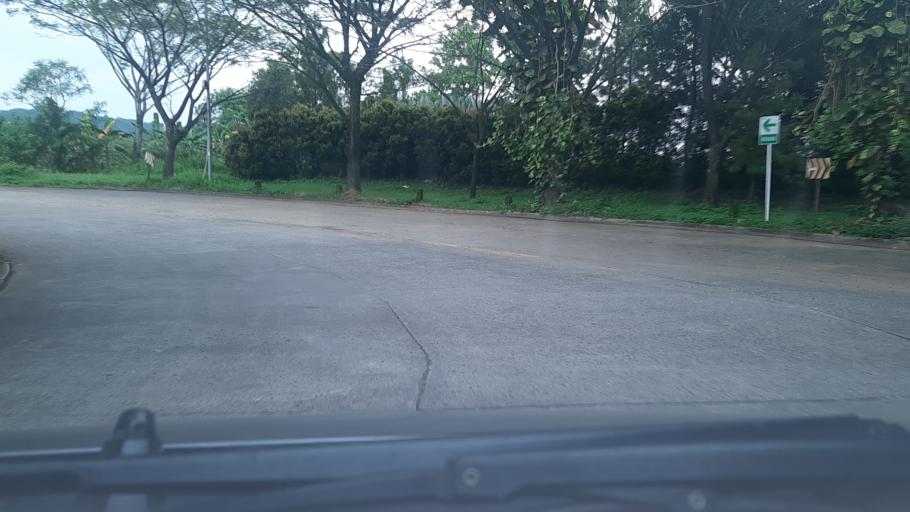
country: ID
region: West Java
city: Citeureup
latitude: -6.5733
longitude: 106.8909
